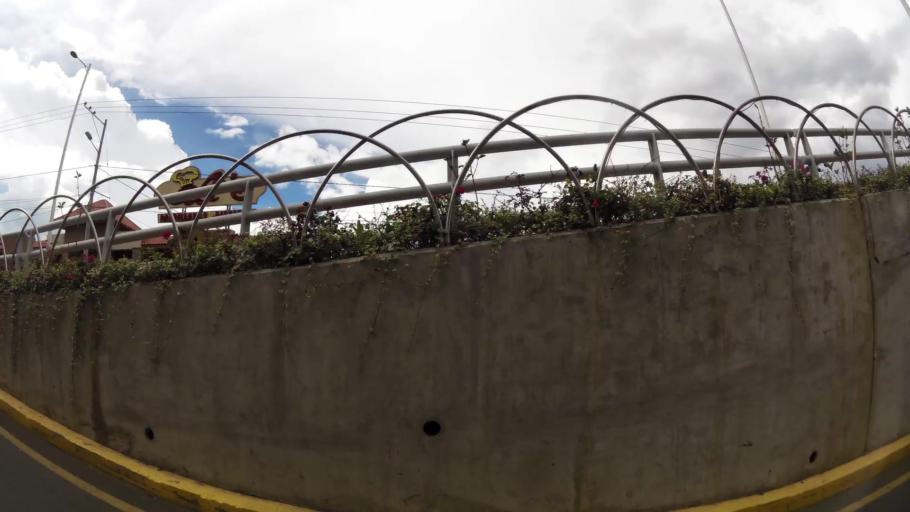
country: EC
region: Tungurahua
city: Ambato
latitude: -1.2644
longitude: -78.6283
